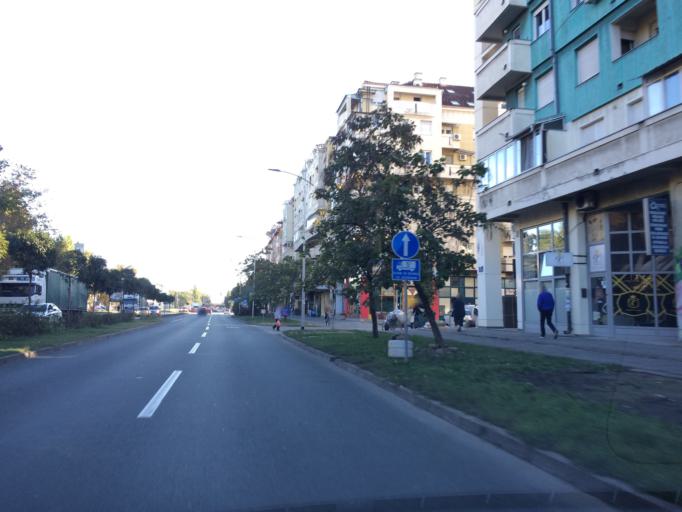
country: RS
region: Autonomna Pokrajina Vojvodina
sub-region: Juznobacki Okrug
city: Novi Sad
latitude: 45.2628
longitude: 19.8149
